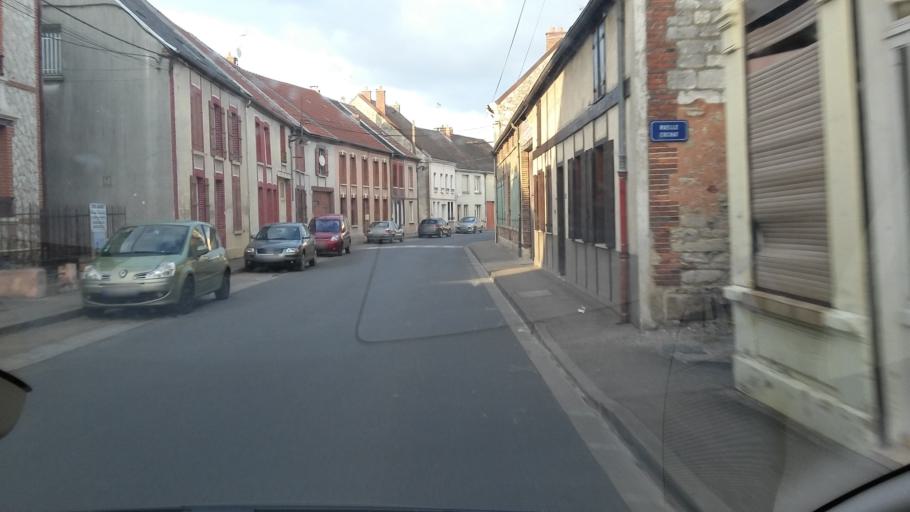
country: FR
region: Champagne-Ardenne
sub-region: Departement de la Marne
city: Fere-Champenoise
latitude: 48.7537
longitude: 3.9871
